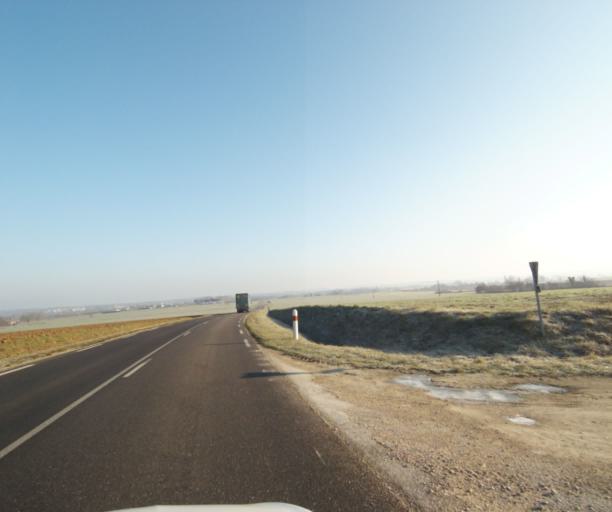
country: FR
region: Champagne-Ardenne
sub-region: Departement de la Haute-Marne
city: Montier-en-Der
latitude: 48.4595
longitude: 4.7511
